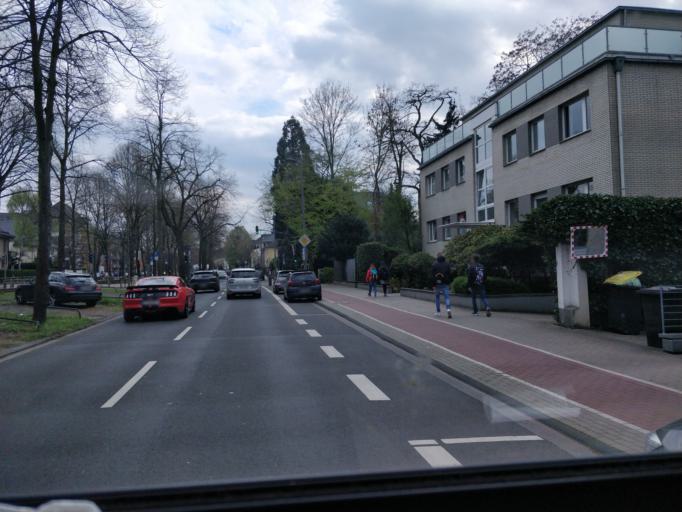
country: DE
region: North Rhine-Westphalia
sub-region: Regierungsbezirk Koln
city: Neuehrenfeld
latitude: 50.9337
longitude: 6.9077
